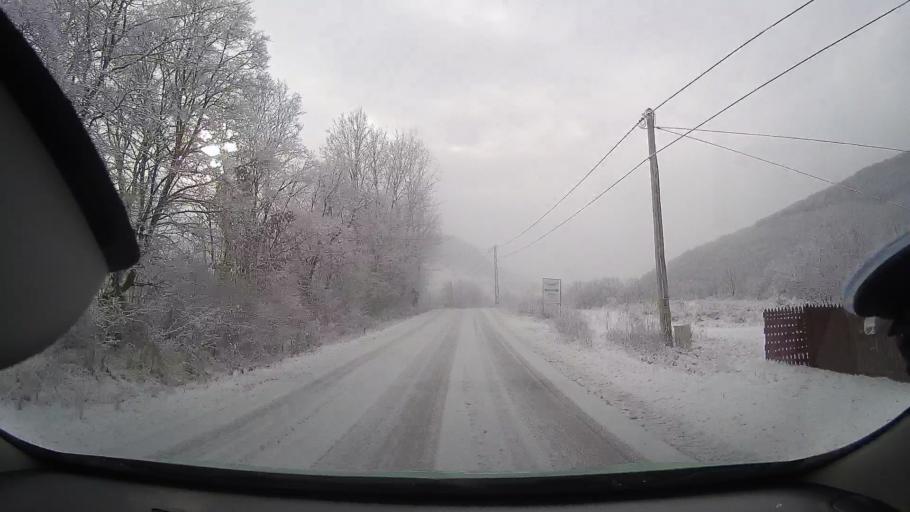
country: RO
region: Alba
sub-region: Comuna Rimetea
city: Rimetea
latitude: 46.4742
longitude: 23.5847
